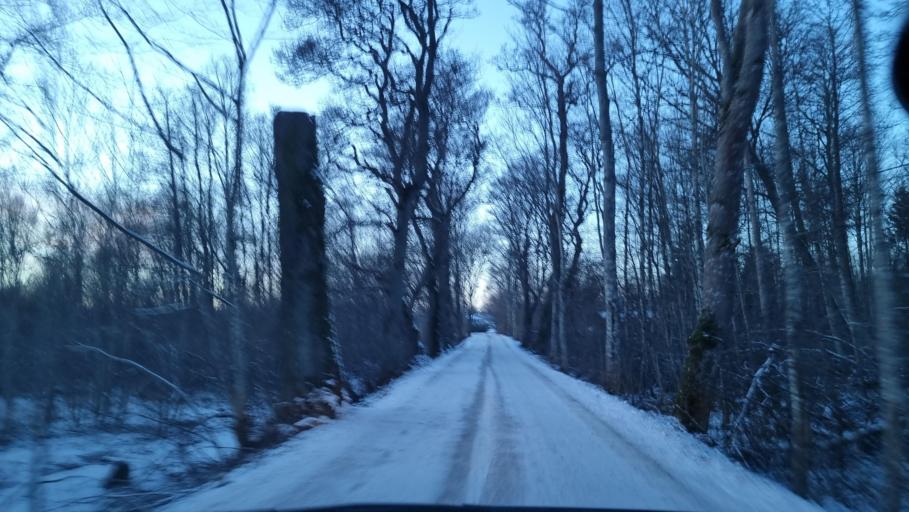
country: SE
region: Stockholm
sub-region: Vallentuna Kommun
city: Vallentuna
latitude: 59.5833
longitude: 18.1143
